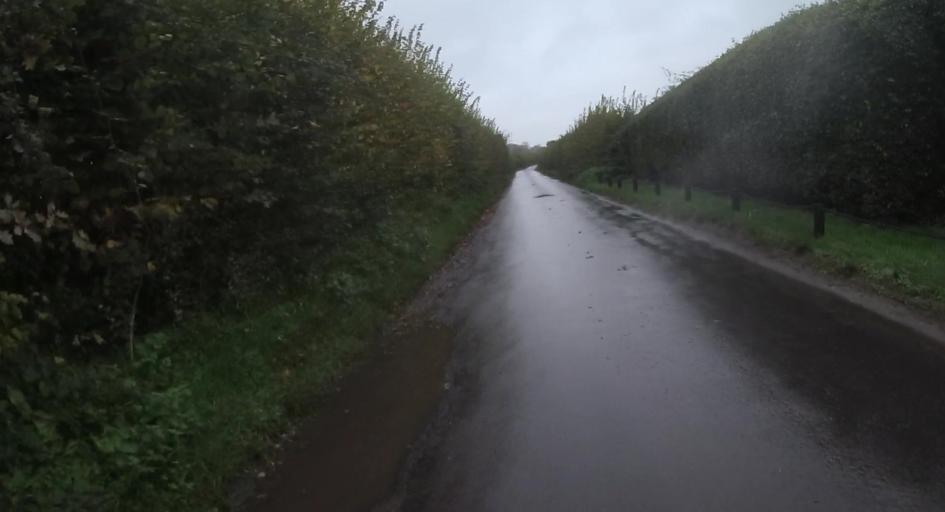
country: GB
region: England
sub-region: Surrey
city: Farnham
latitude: 51.2072
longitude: -0.8533
